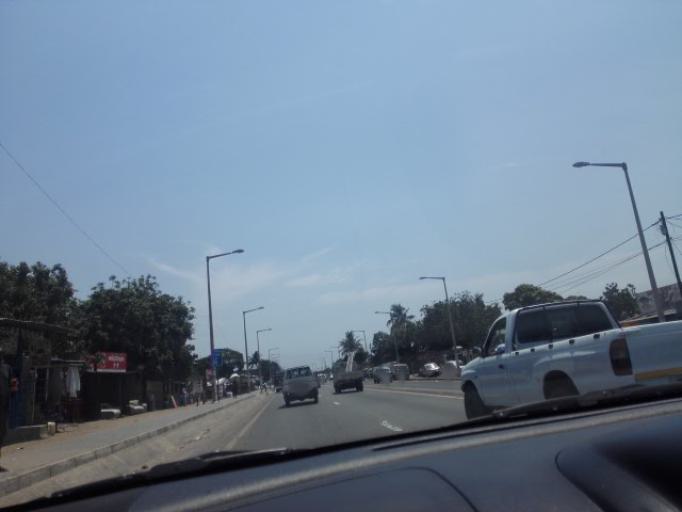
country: MZ
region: Maputo City
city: Maputo
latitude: -25.9242
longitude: 32.5599
